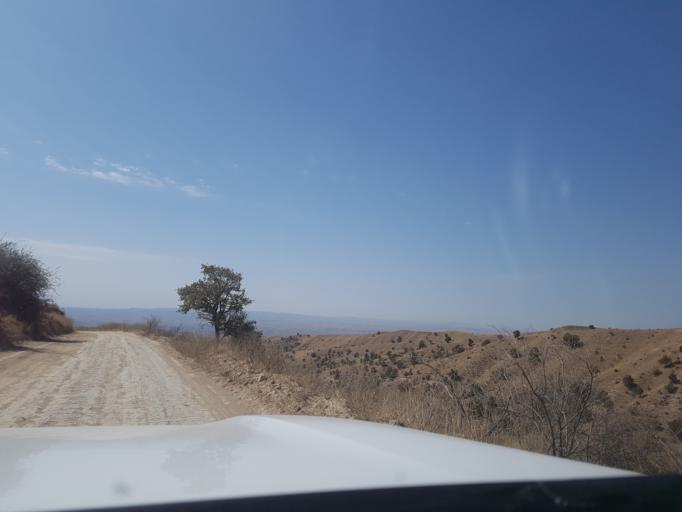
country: TM
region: Ahal
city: Baharly
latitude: 38.2950
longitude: 56.9352
